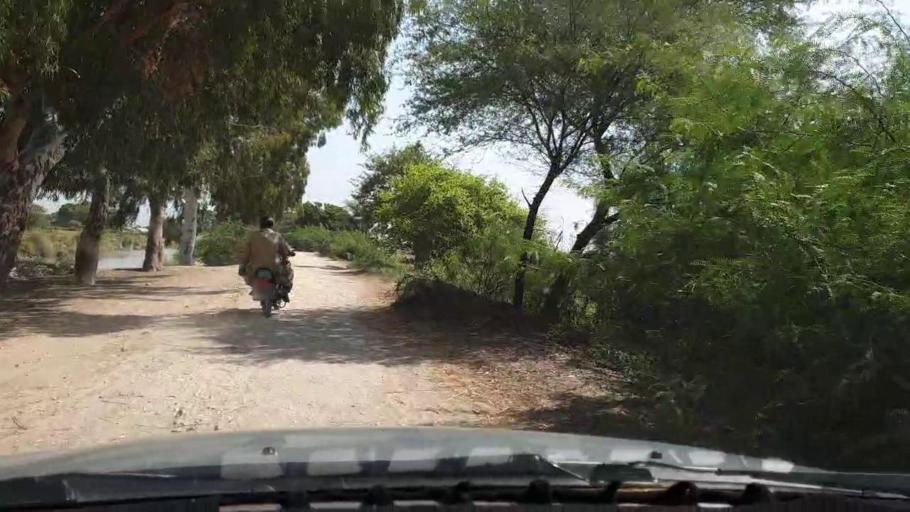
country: PK
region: Sindh
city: Tando Muhammad Khan
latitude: 25.1019
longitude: 68.5898
